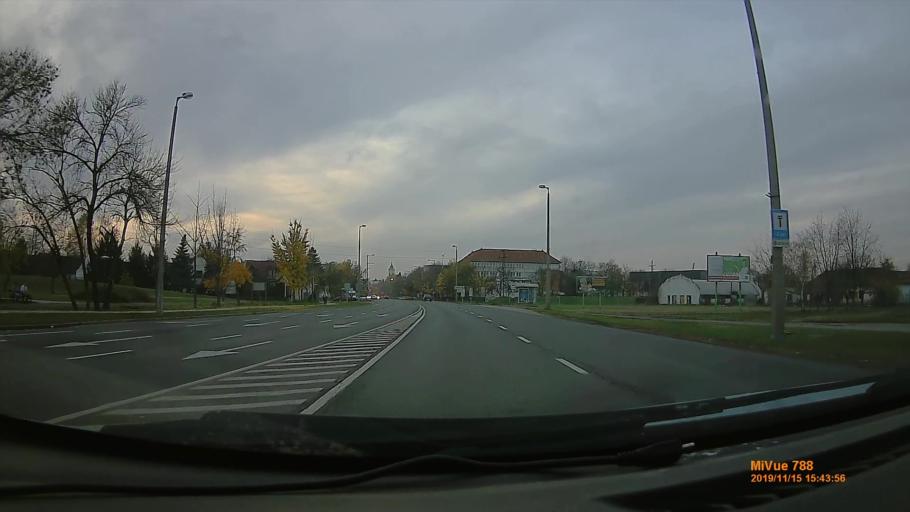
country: HU
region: Bekes
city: Bekescsaba
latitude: 46.6817
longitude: 21.1121
